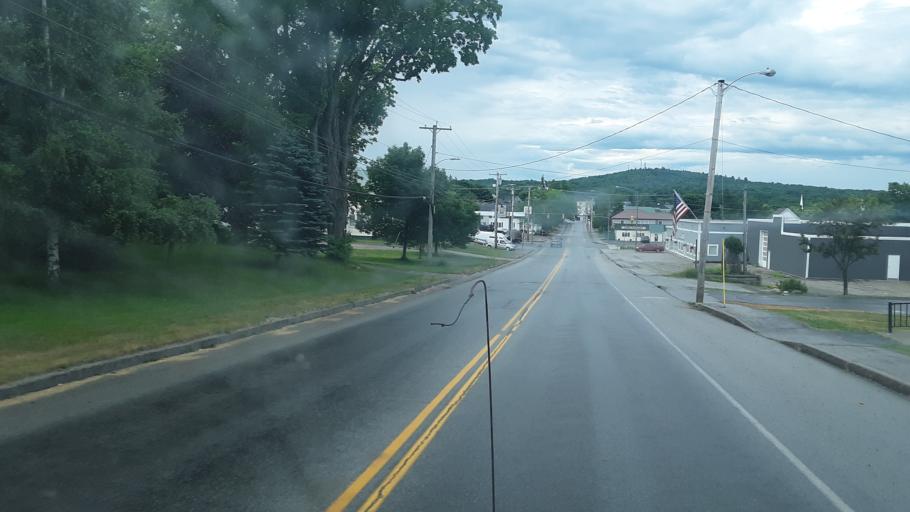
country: US
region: Maine
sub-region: Penobscot County
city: Lincoln
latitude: 45.3693
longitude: -68.5030
